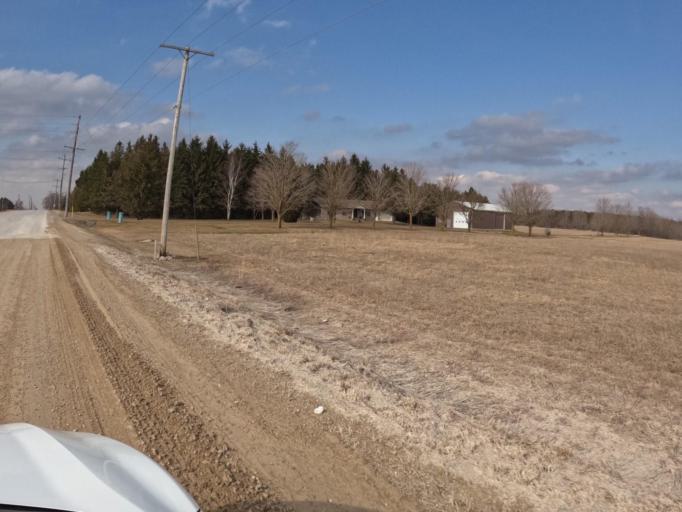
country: CA
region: Ontario
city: Shelburne
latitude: 43.9014
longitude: -80.3016
